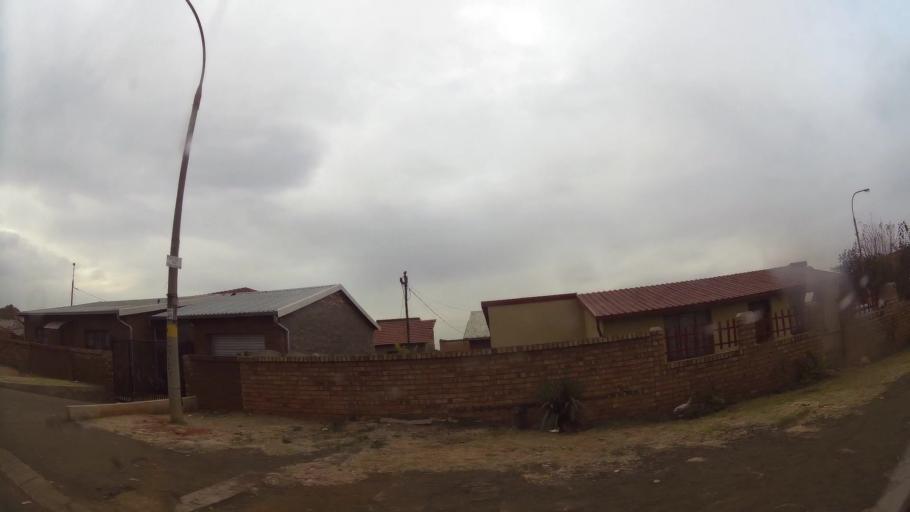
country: ZA
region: Gauteng
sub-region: Ekurhuleni Metropolitan Municipality
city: Germiston
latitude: -26.3770
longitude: 28.1295
